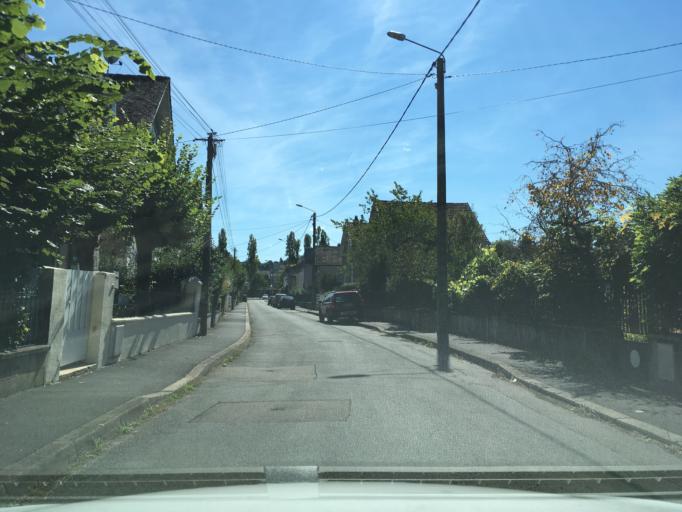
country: FR
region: Limousin
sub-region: Departement de la Correze
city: Brive-la-Gaillarde
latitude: 45.1615
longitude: 1.5455
